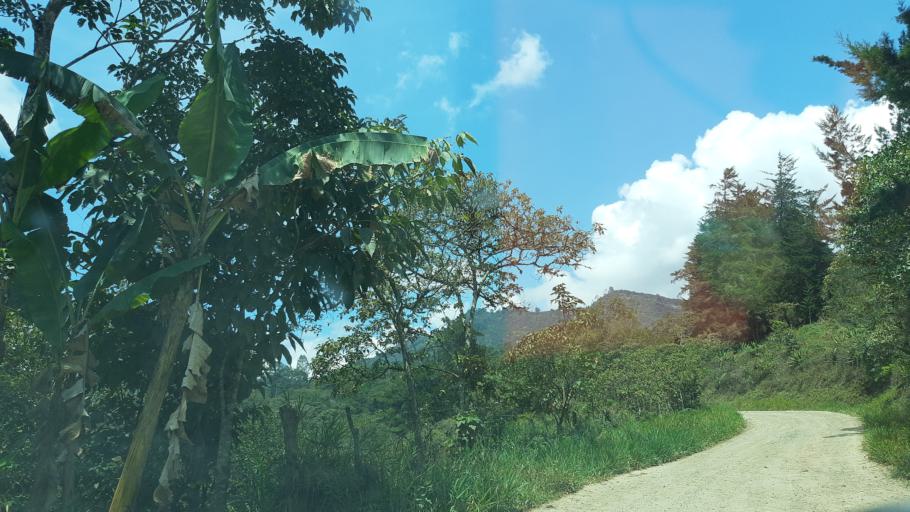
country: CO
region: Boyaca
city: Chinavita
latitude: 5.1287
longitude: -73.3707
